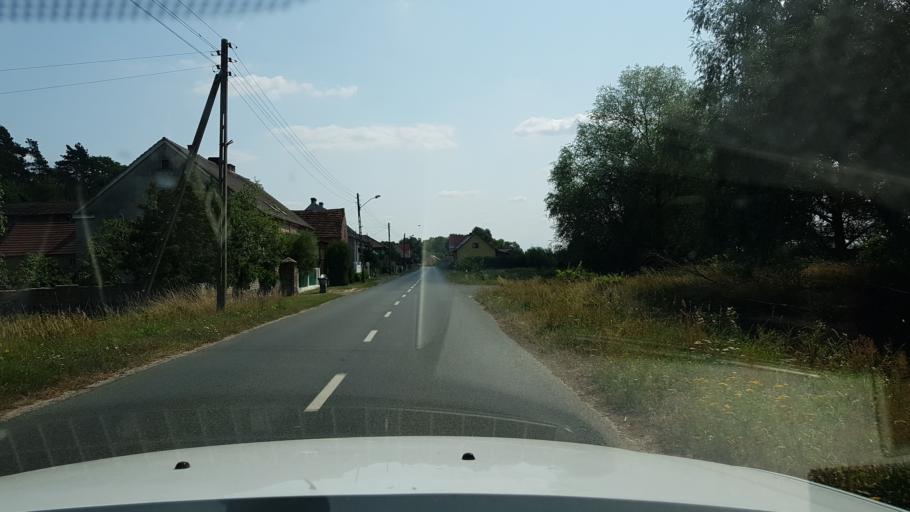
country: PL
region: West Pomeranian Voivodeship
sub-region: Powiat gryfinski
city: Cedynia
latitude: 52.8106
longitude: 14.2426
